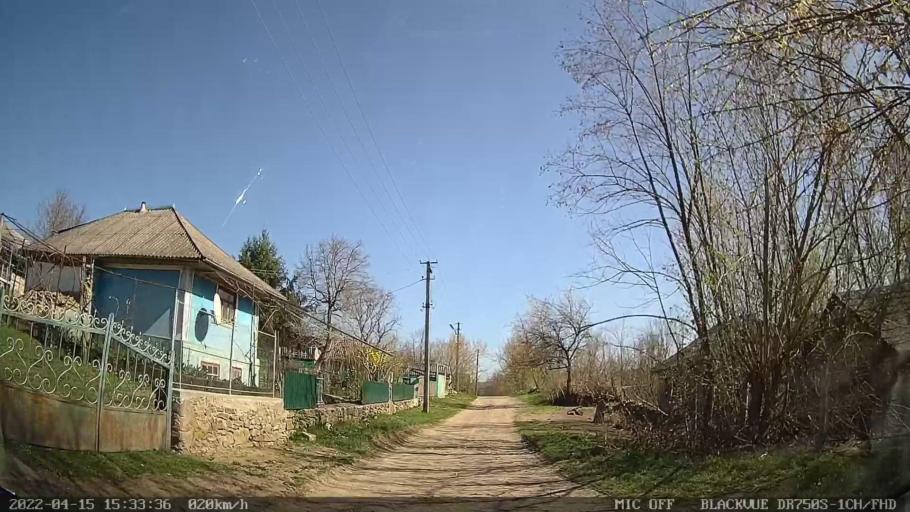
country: MD
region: Raionul Ocnita
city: Otaci
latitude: 48.3493
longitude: 27.9242
